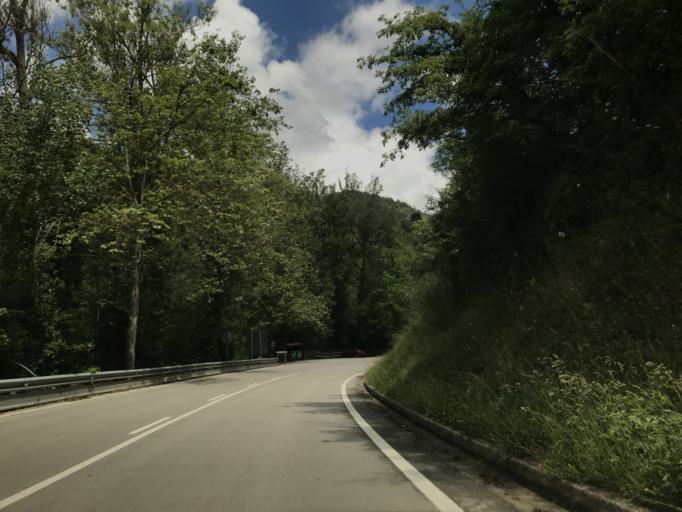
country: ES
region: Cantabria
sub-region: Provincia de Cantabria
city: Camaleno
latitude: 43.1281
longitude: -4.7271
